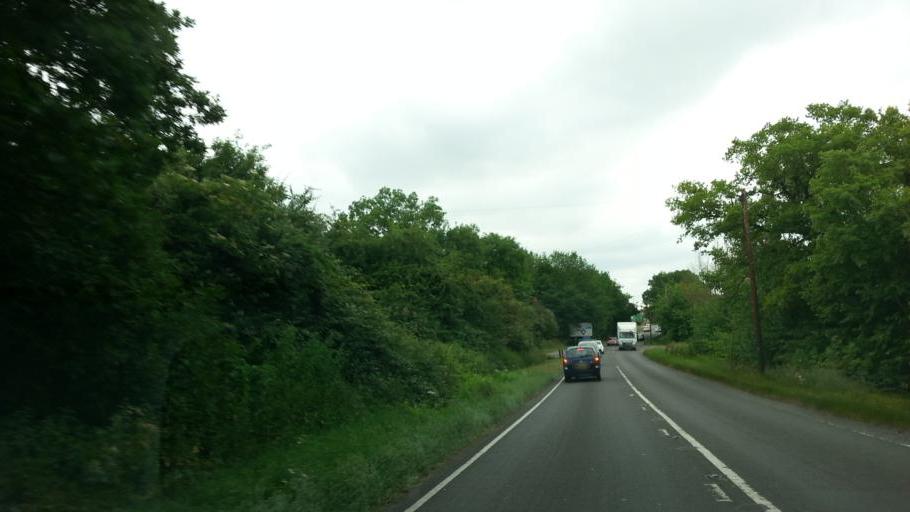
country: GB
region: England
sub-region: Cambridgeshire
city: Papworth Everard
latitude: 52.2384
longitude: -0.1102
